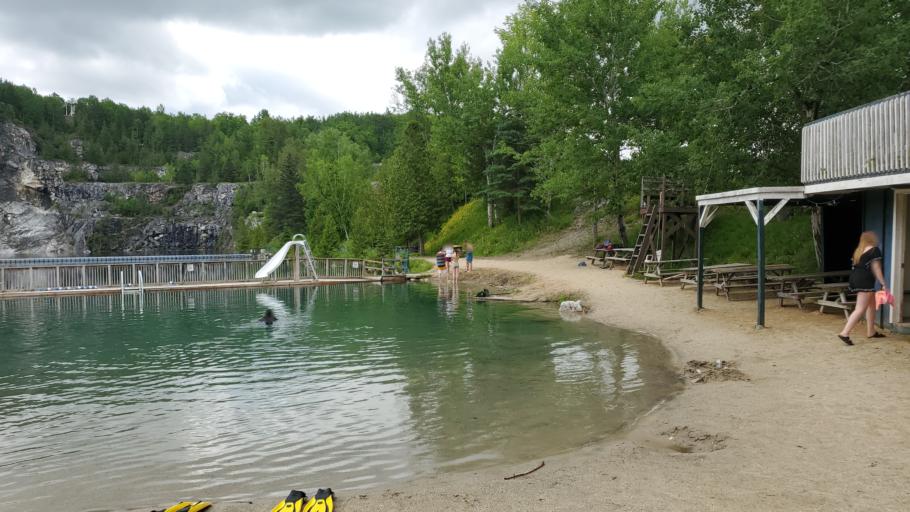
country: CA
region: Quebec
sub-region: Outaouais
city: Wakefield
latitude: 45.6142
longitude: -75.9095
